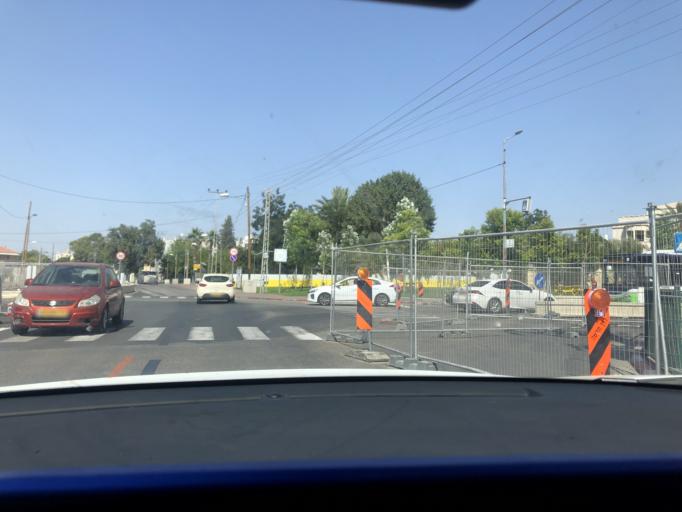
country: IL
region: Central District
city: Lod
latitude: 31.9447
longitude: 34.8772
